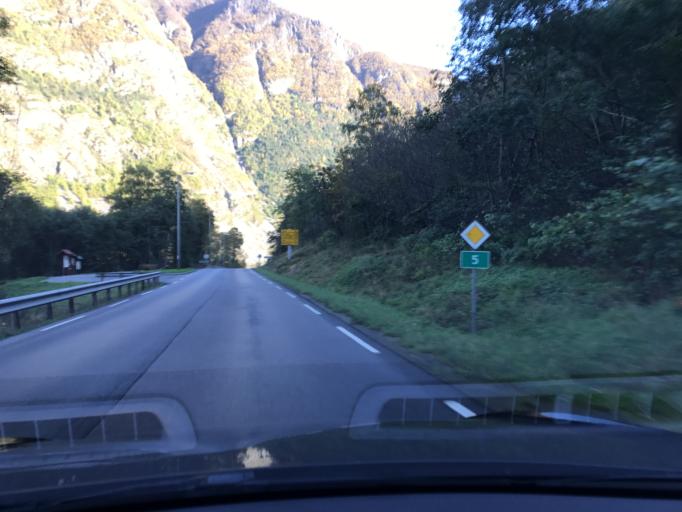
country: NO
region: Sogn og Fjordane
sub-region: Laerdal
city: Laerdalsoyri
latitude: 61.0997
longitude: 7.5107
